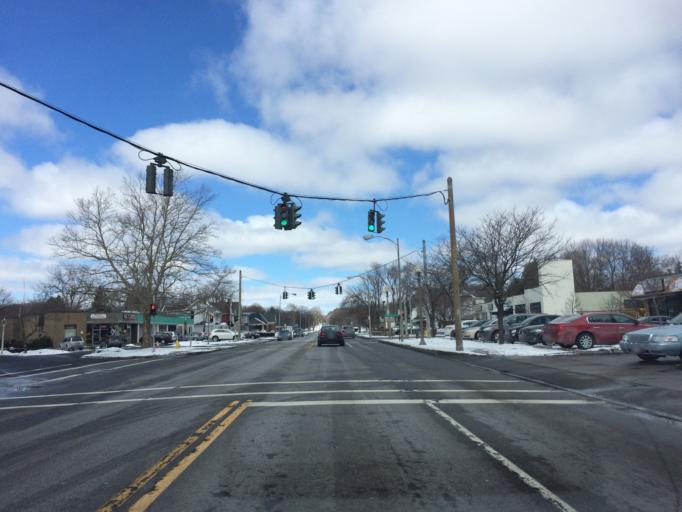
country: US
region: New York
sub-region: Monroe County
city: Brighton
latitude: 43.1291
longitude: -77.5675
